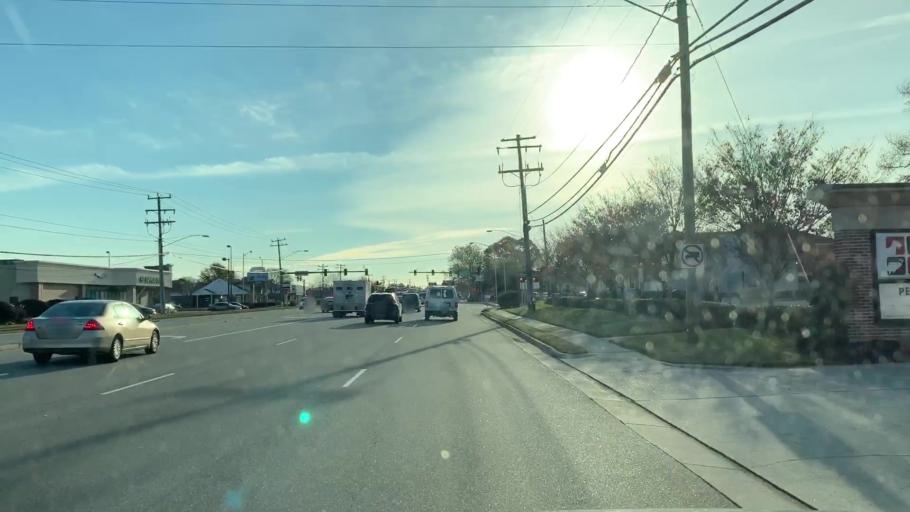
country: US
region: Virginia
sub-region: City of Chesapeake
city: Chesapeake
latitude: 36.8003
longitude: -76.1809
